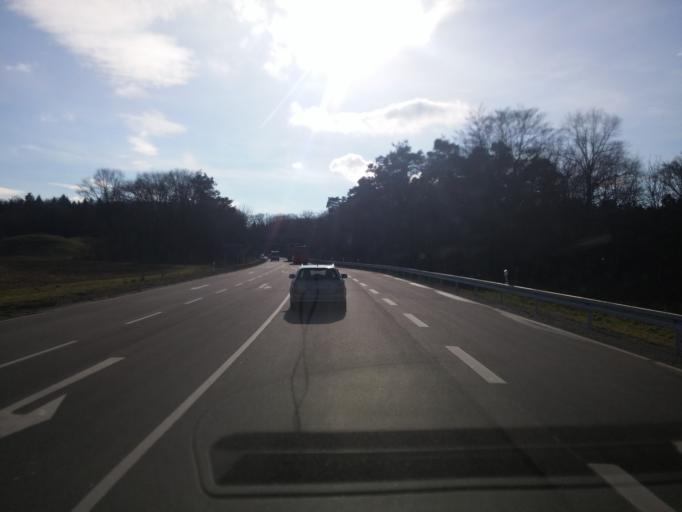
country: DE
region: Baden-Wuerttemberg
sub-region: Karlsruhe Region
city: Eggenstein-Leopoldshafen
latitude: 49.0690
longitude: 8.4537
